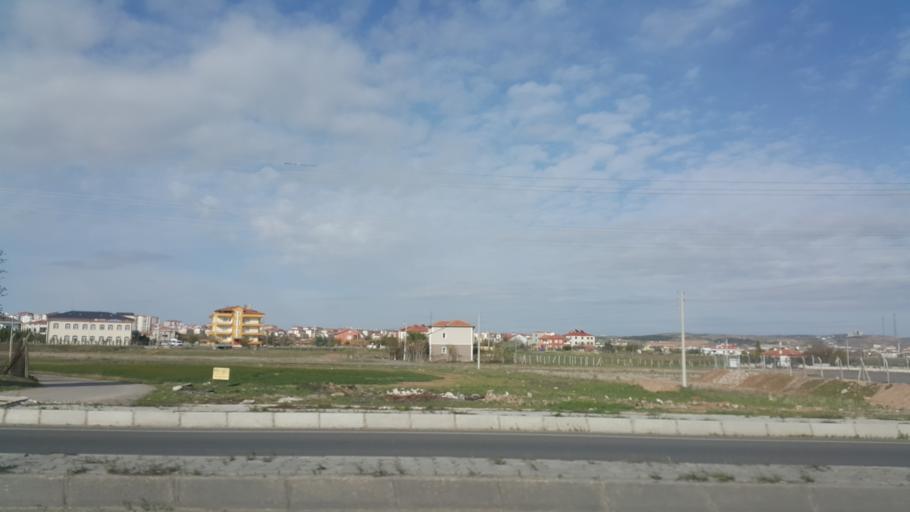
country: TR
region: Aksaray
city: Aksaray
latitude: 38.4024
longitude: 33.9816
